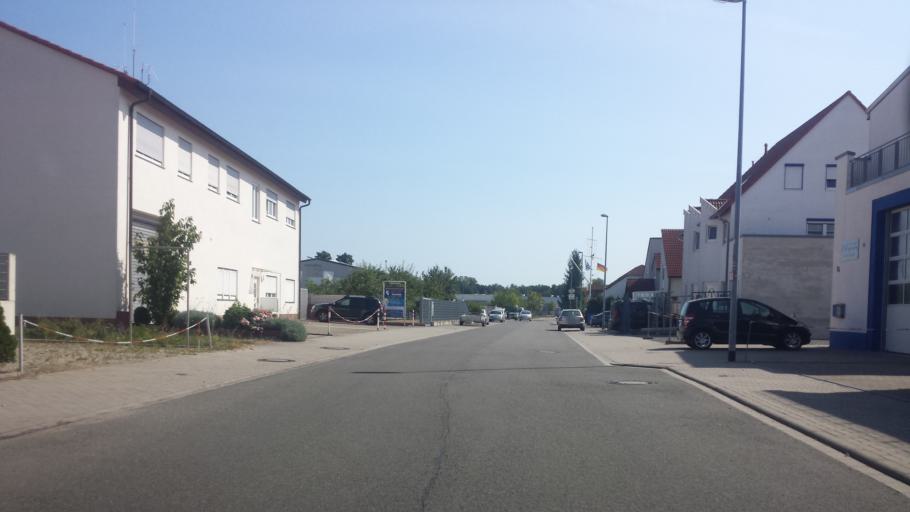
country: DE
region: Rheinland-Pfalz
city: Hassloch
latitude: 49.3497
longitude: 8.2393
